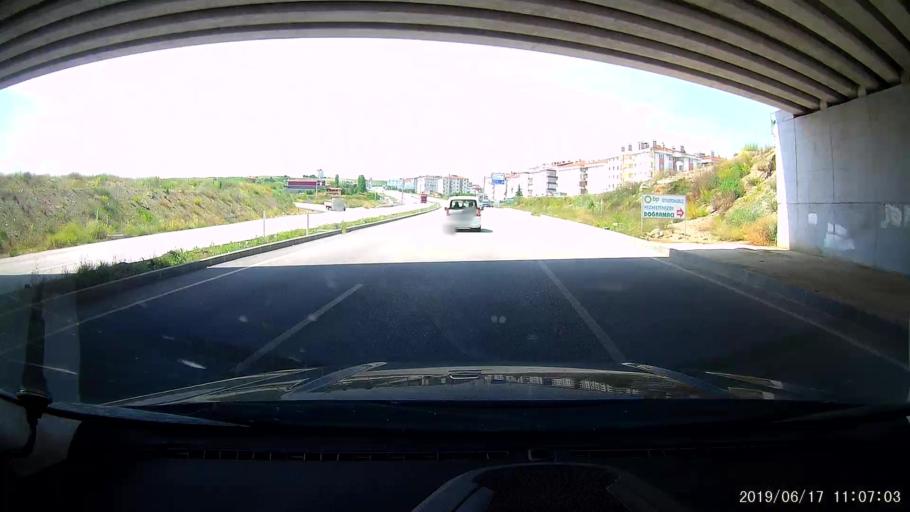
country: TR
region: Kastamonu
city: Tosya
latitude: 41.0075
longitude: 34.0586
